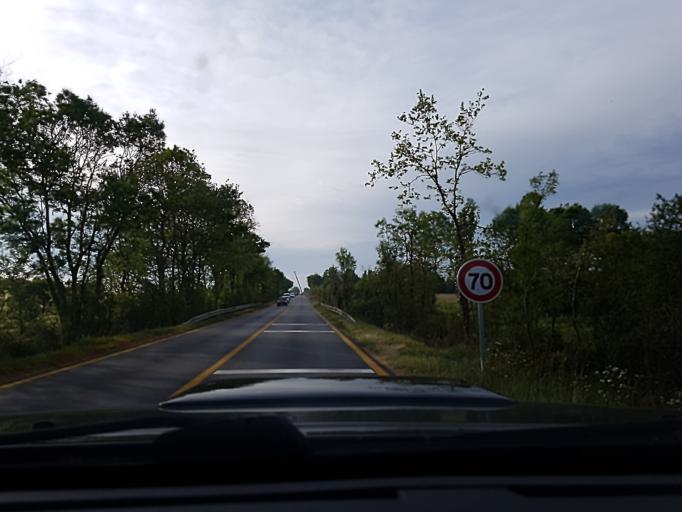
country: FR
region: Pays de la Loire
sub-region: Departement de la Vendee
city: Mache
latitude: 46.7669
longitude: -1.6601
